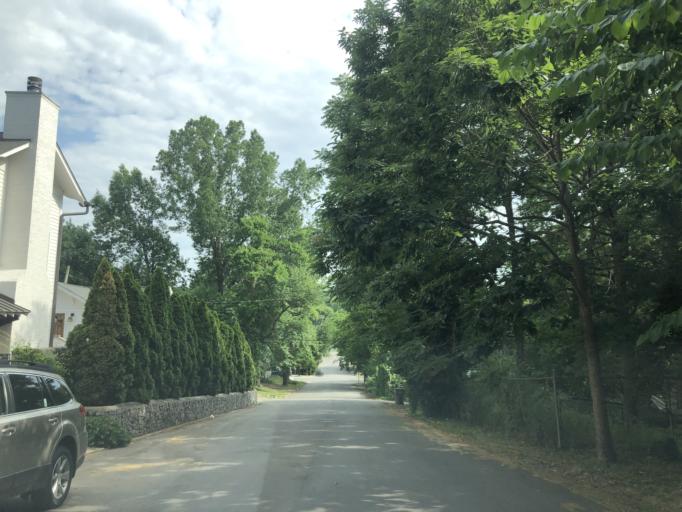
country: US
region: Tennessee
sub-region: Davidson County
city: Oak Hill
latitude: 36.1262
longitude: -86.7983
